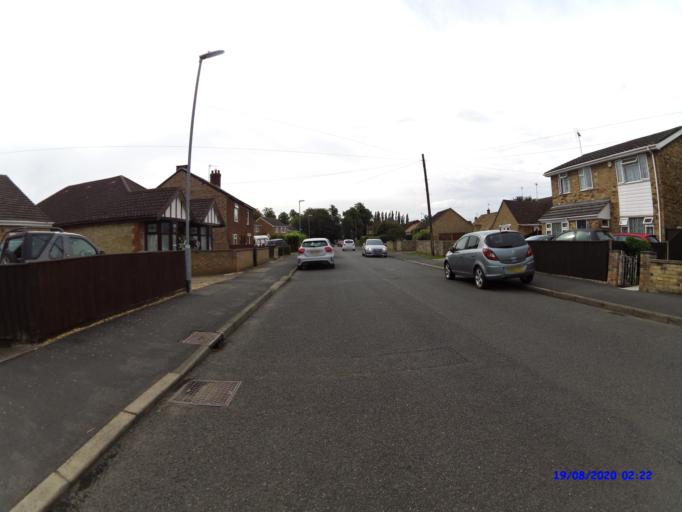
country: GB
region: England
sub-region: Cambridgeshire
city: Ramsey
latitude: 52.4511
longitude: -0.1065
